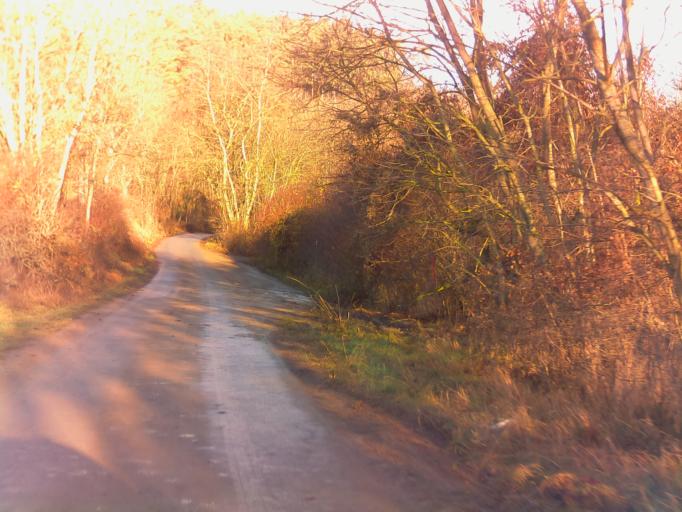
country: DE
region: Thuringia
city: Gumperda
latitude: 50.7974
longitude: 11.5143
